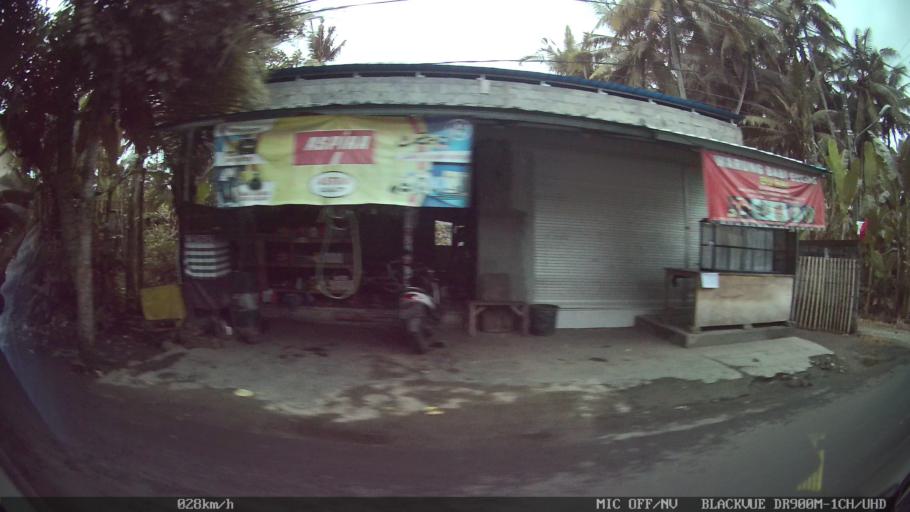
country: ID
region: Bali
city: Banjar Parekan
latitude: -8.5663
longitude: 115.2110
